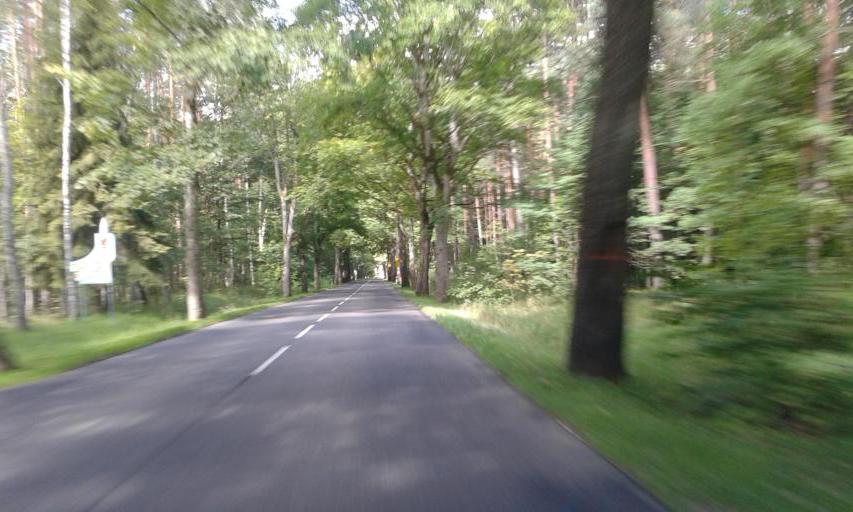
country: PL
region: West Pomeranian Voivodeship
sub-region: Powiat slawienski
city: Slawno
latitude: 54.2473
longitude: 16.6961
